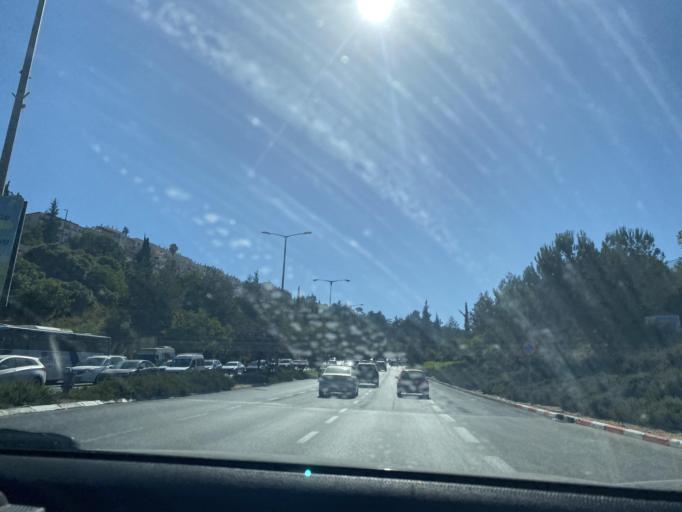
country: PS
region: West Bank
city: Bayt Iksa
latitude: 31.8125
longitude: 35.2007
